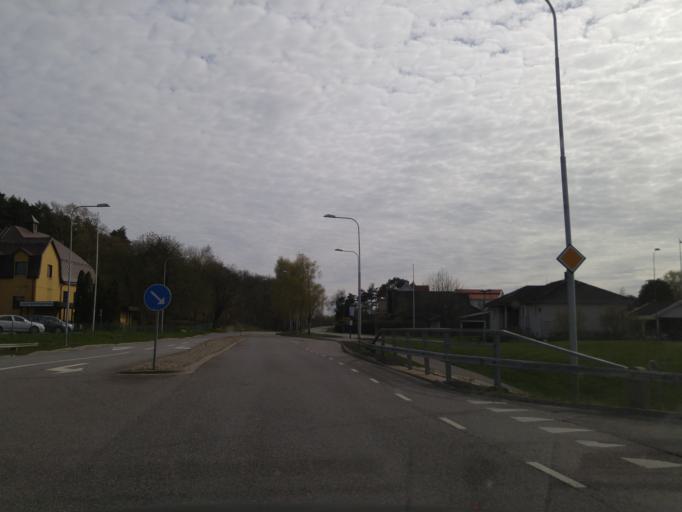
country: SE
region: Vaestra Goetaland
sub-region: Goteborg
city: Majorna
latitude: 57.6599
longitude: 11.8721
